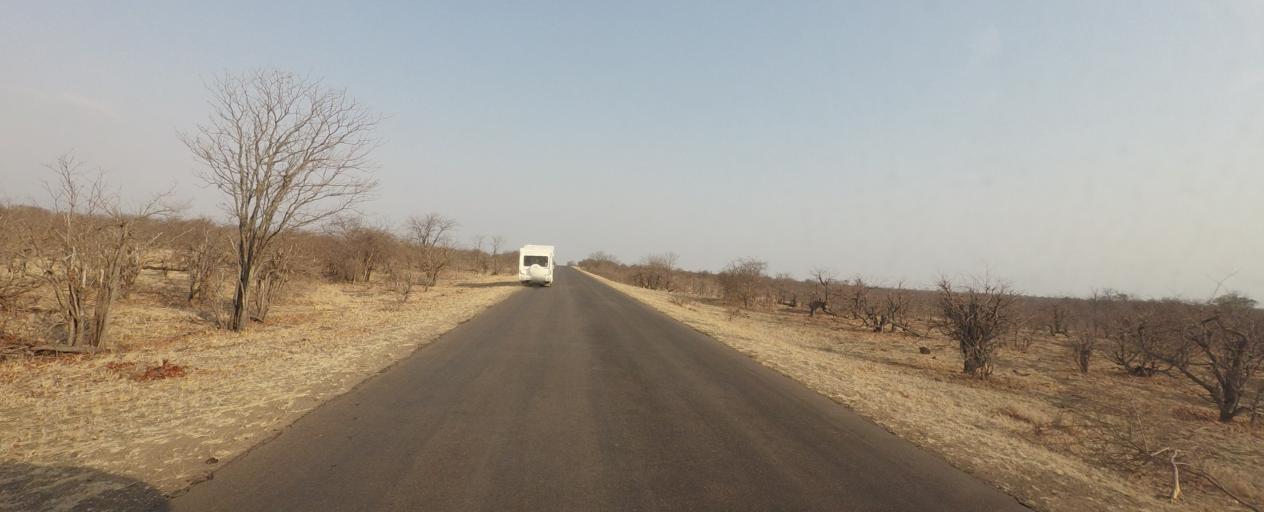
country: ZA
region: Limpopo
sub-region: Mopani District Municipality
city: Giyani
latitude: -23.0840
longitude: 31.4198
